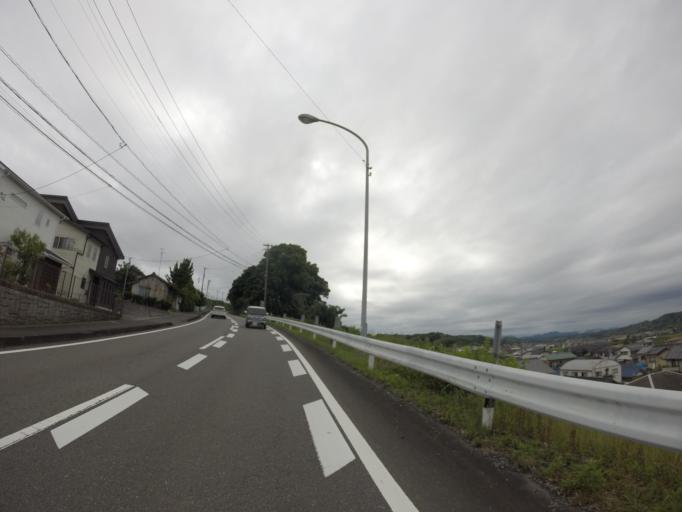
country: JP
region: Shizuoka
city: Sagara
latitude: 34.7388
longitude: 138.2156
